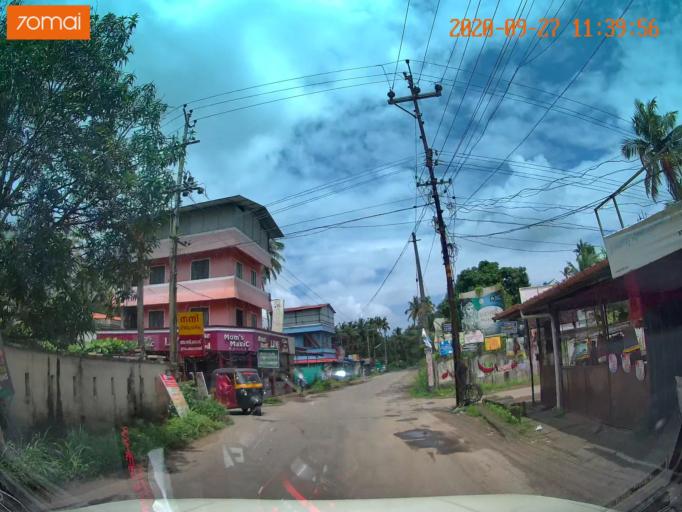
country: IN
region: Kerala
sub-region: Thrissur District
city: Thanniyam
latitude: 10.4659
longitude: 76.1175
